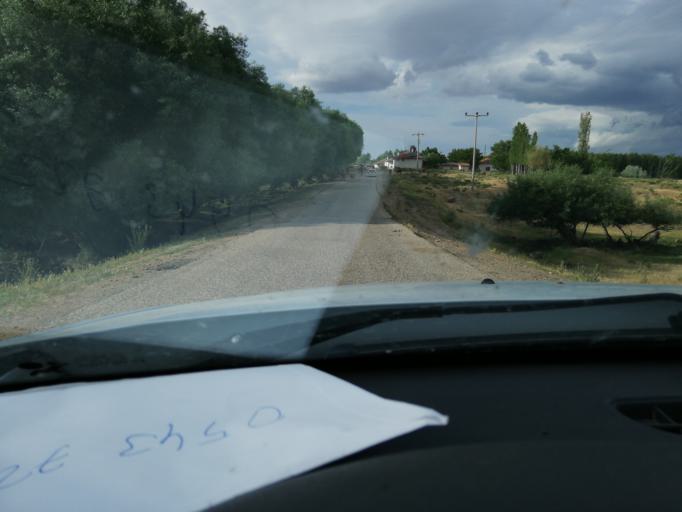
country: TR
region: Kirsehir
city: Kirsehir
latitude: 39.0220
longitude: 34.1237
